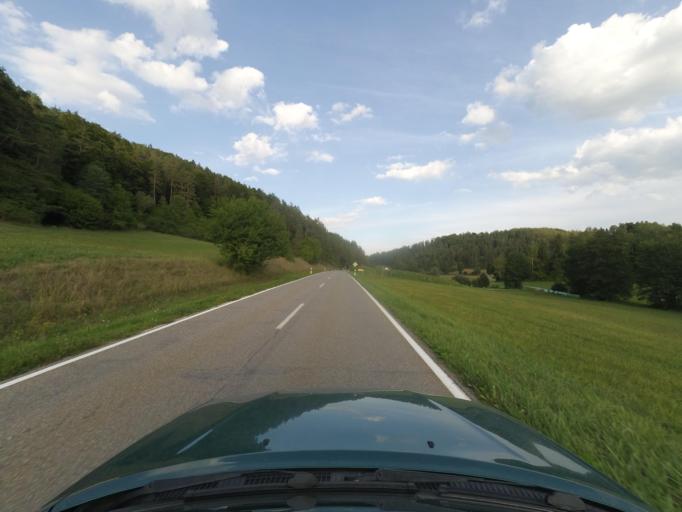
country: DE
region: Bavaria
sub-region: Upper Palatinate
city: Hirschbach
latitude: 49.5669
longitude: 11.5704
